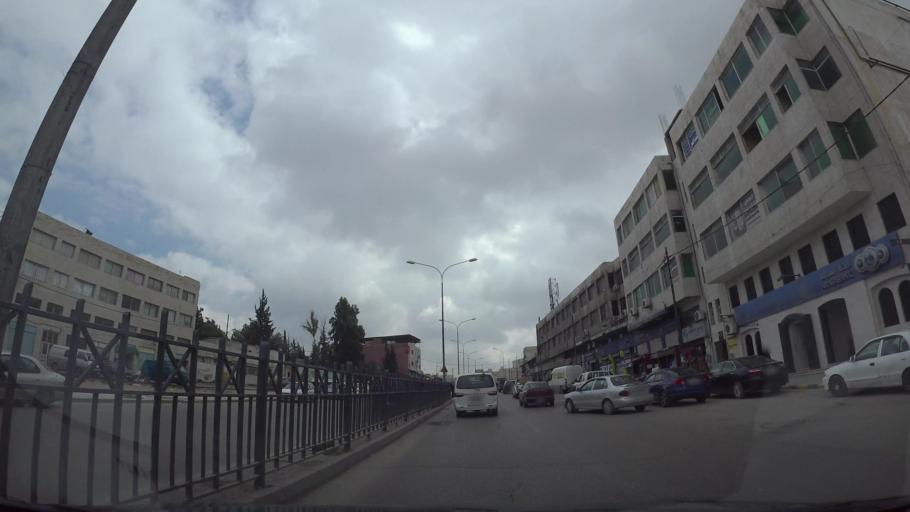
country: JO
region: Amman
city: Al Quwaysimah
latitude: 31.9147
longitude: 35.9387
